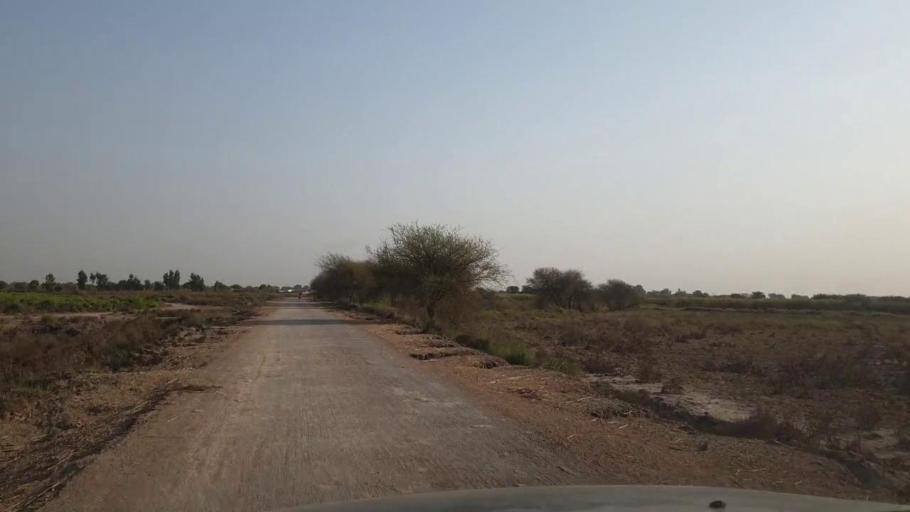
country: PK
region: Sindh
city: Bulri
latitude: 24.9489
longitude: 68.3420
